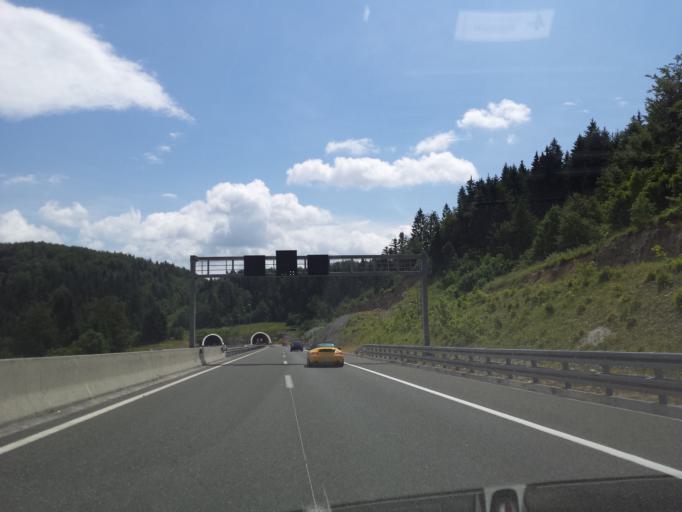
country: HR
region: Primorsko-Goranska
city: Vrbovsko
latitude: 45.3735
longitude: 15.0032
